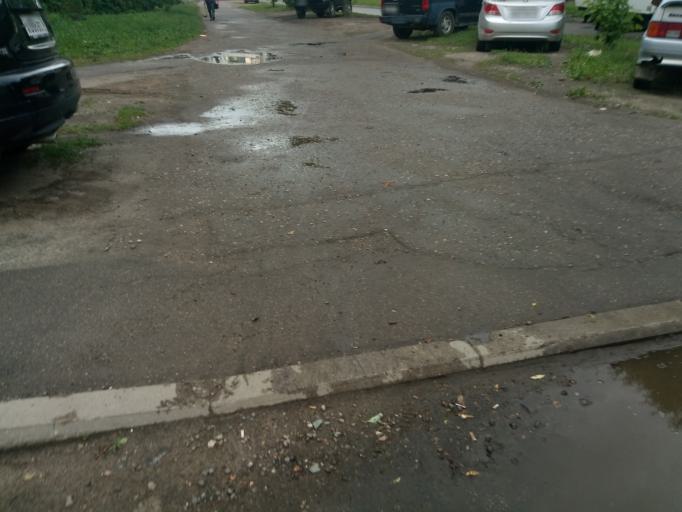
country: RU
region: Jaroslavl
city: Yaroslavl
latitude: 57.6499
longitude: 39.9588
